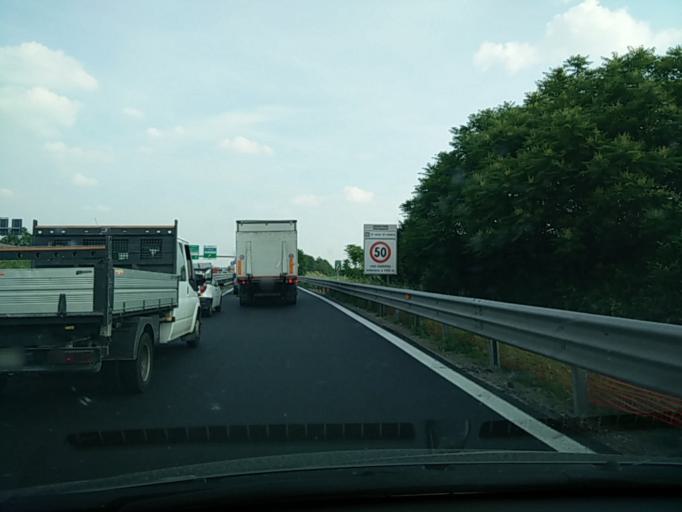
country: IT
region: Lombardy
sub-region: Citta metropolitana di Milano
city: Figino
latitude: 45.5075
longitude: 9.0636
